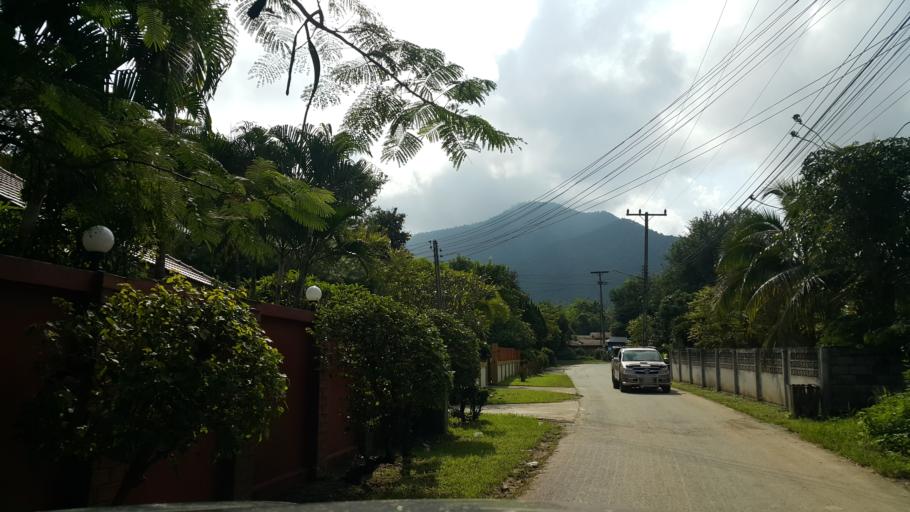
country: TH
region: Chiang Mai
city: Mae On
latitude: 18.7395
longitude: 99.2326
